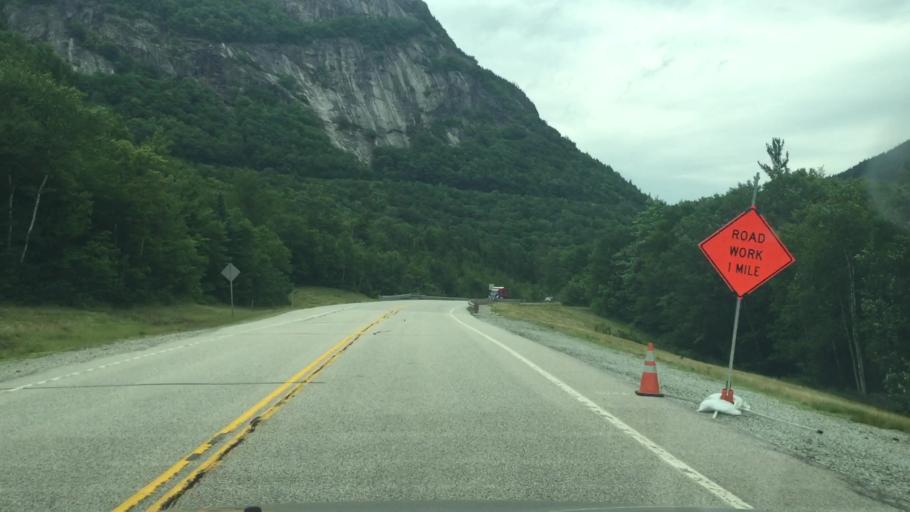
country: US
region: New Hampshire
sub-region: Grafton County
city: Deerfield
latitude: 44.1965
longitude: -71.4069
